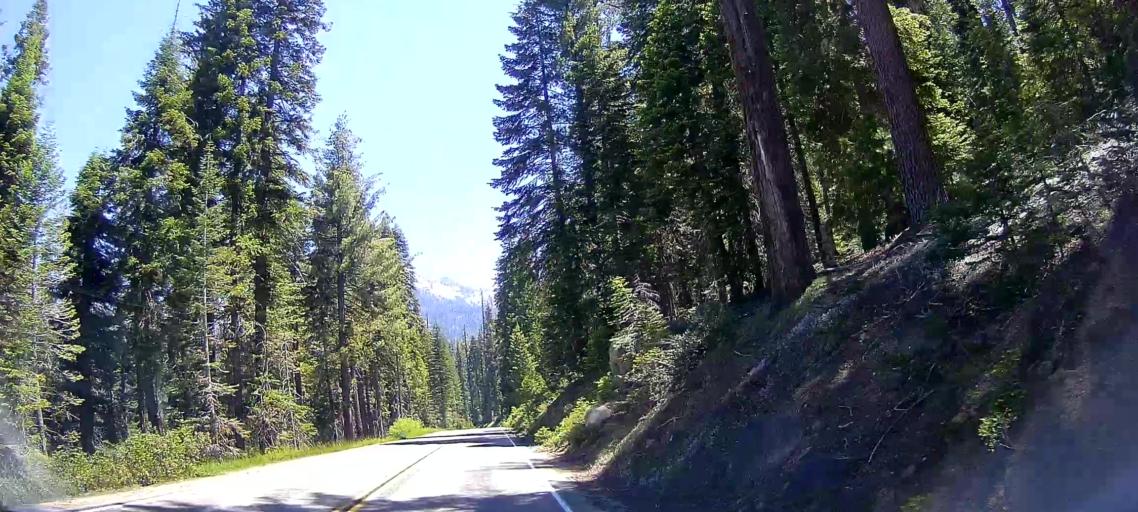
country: US
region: California
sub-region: Tulare County
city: Three Rivers
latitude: 36.5979
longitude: -118.7472
